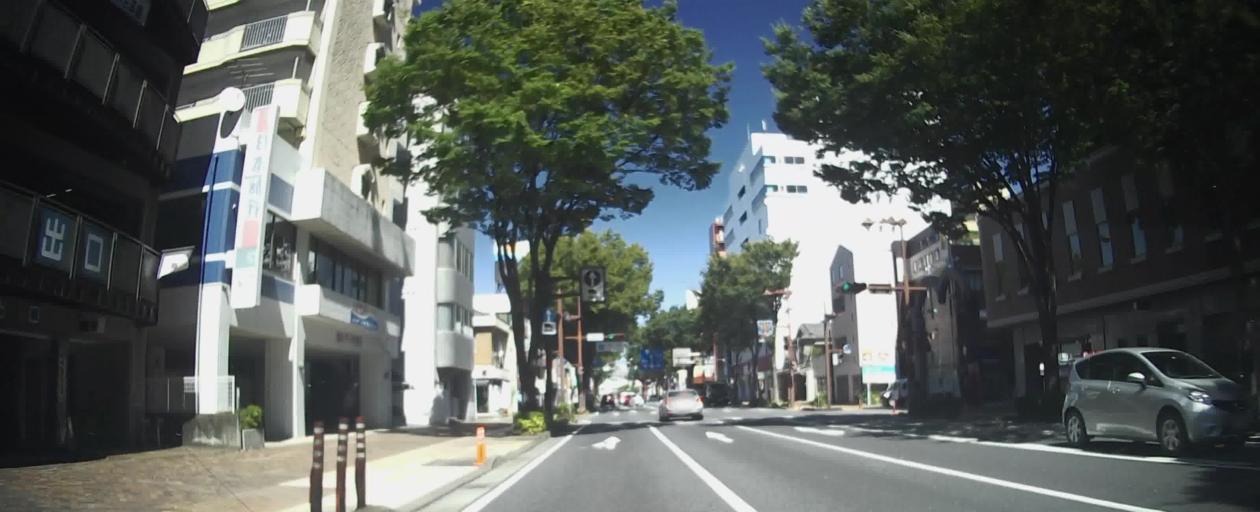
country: JP
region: Gunma
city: Maebashi-shi
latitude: 36.3926
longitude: 139.0680
